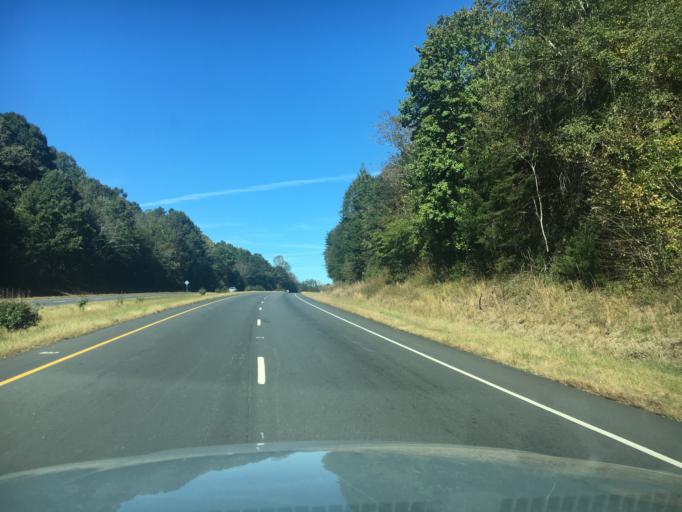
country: US
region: North Carolina
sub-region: Rutherford County
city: Spindale
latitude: 35.3497
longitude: -81.9389
